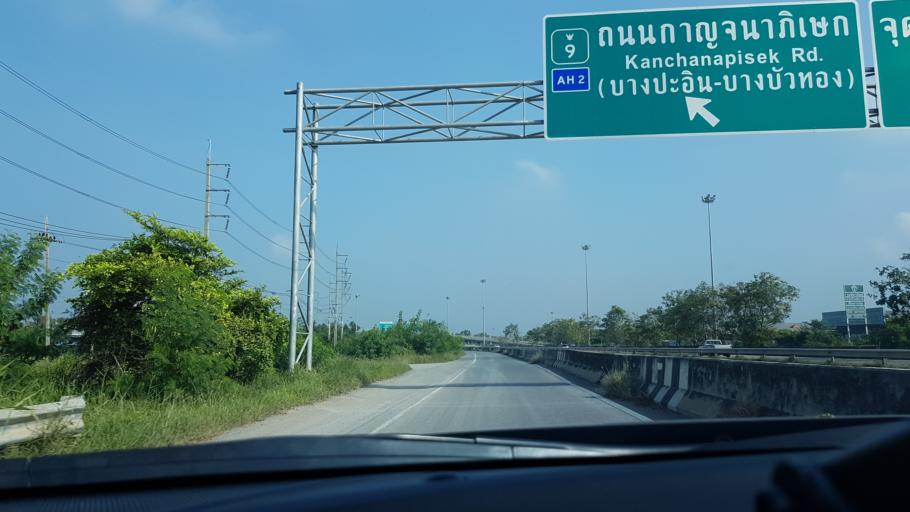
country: TH
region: Phra Nakhon Si Ayutthaya
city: Bang Pa-in
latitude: 14.1516
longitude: 100.5687
